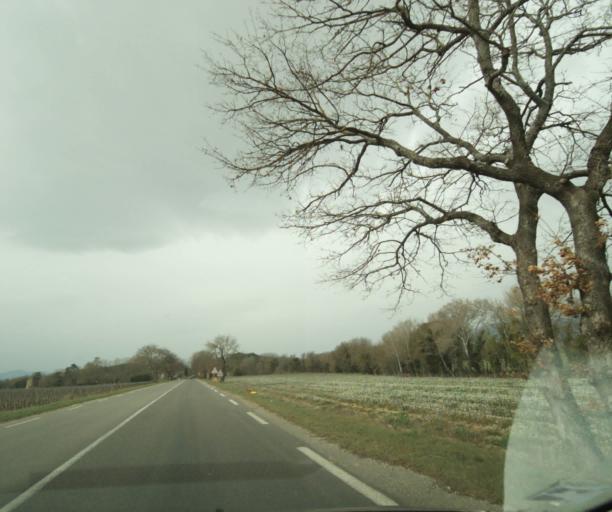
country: FR
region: Provence-Alpes-Cote d'Azur
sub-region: Departement du Var
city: Pourrieres
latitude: 43.4826
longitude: 5.7036
